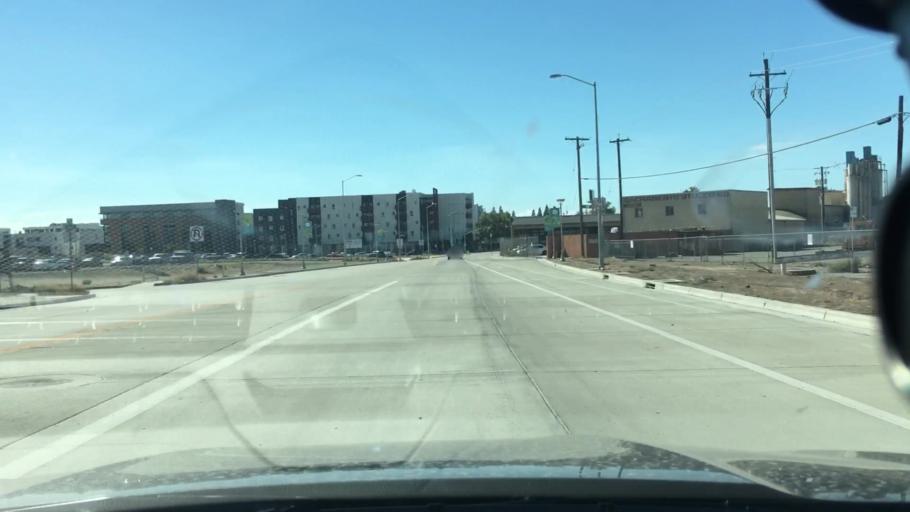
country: US
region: California
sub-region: Yolo County
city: West Sacramento
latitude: 38.5785
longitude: -121.5162
